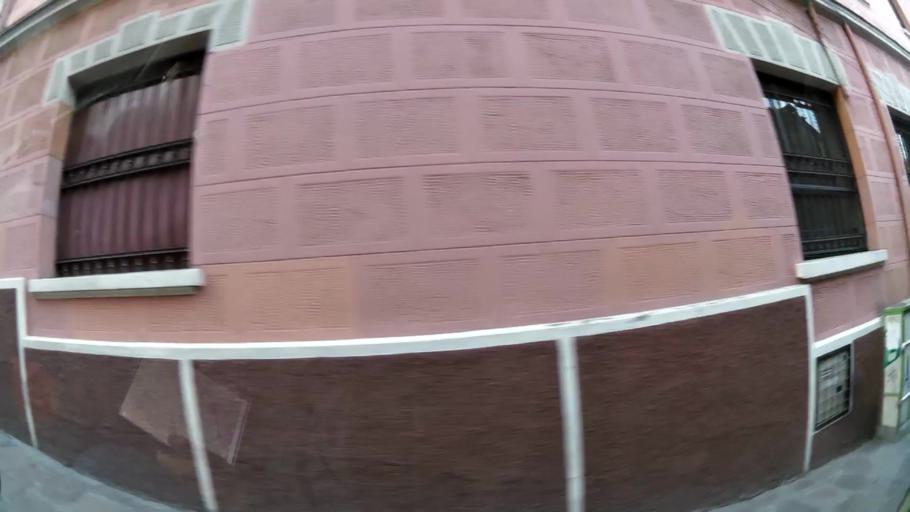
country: BO
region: La Paz
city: La Paz
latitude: -16.4965
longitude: -68.1316
